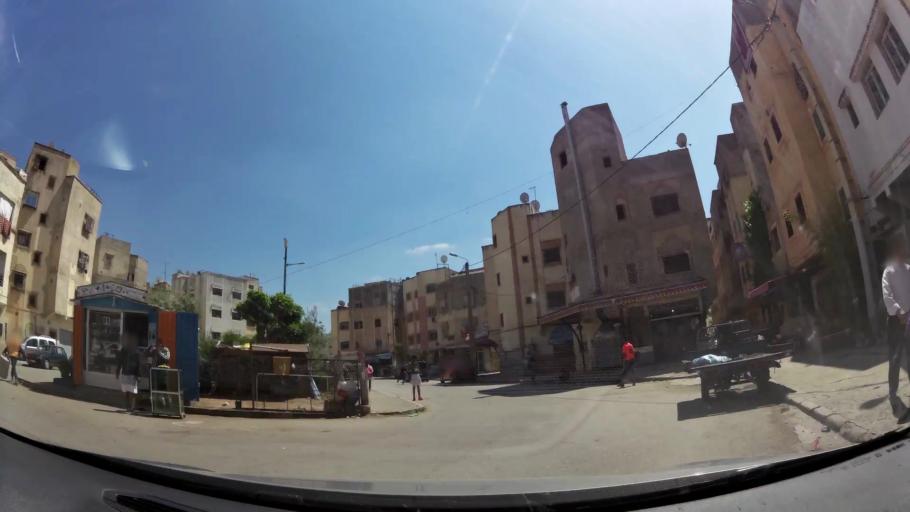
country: MA
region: Fes-Boulemane
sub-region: Fes
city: Fes
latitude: 34.0115
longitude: -5.0280
